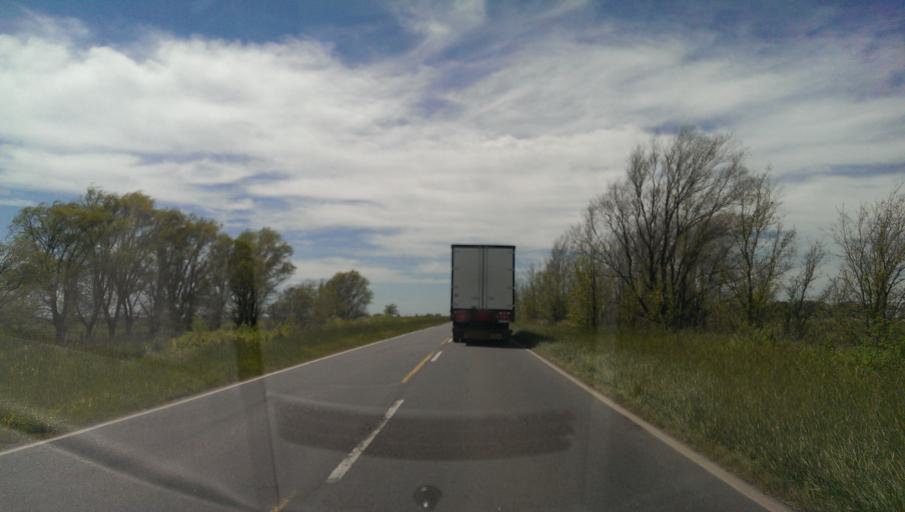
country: AR
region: Buenos Aires
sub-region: Partido de Laprida
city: Laprida
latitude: -37.3603
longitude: -60.9546
